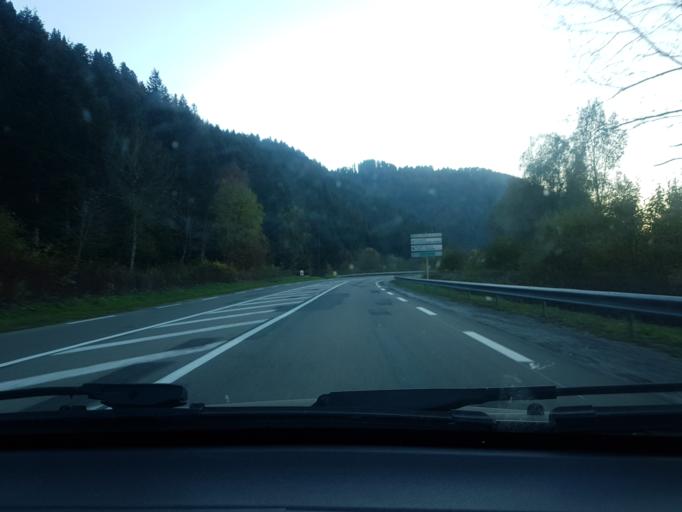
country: FR
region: Franche-Comte
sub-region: Departement du Doubs
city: Villers-le-Lac
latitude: 47.0531
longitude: 6.6716
